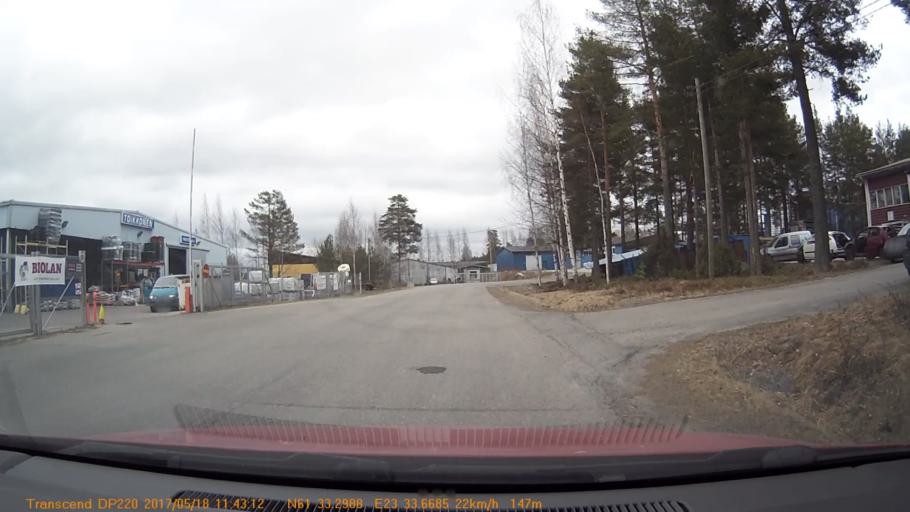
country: FI
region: Pirkanmaa
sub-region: Tampere
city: Yloejaervi
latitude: 61.5549
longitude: 23.5609
